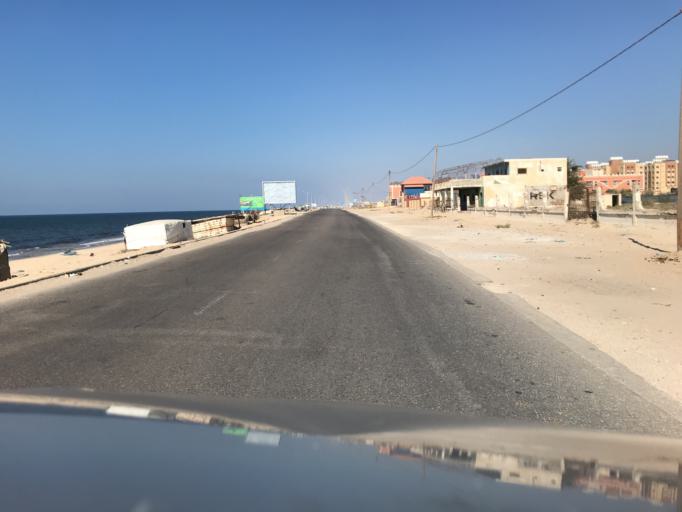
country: PS
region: Gaza Strip
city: An Nusayrat
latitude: 31.4680
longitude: 34.3803
